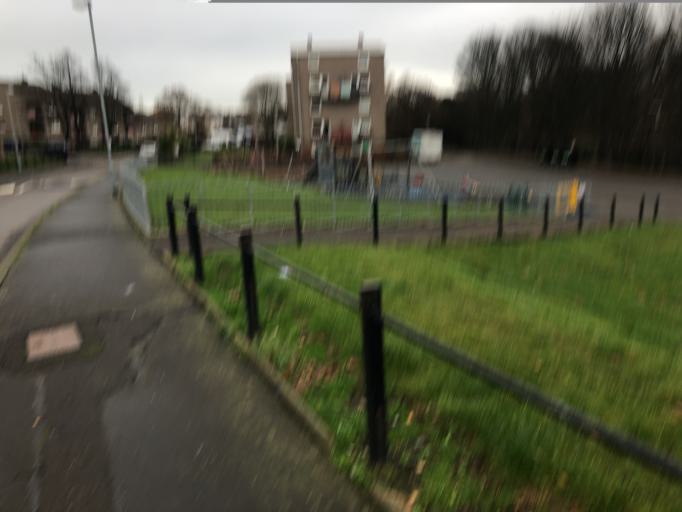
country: GB
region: Scotland
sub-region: West Lothian
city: Seafield
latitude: 55.9489
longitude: -3.1336
